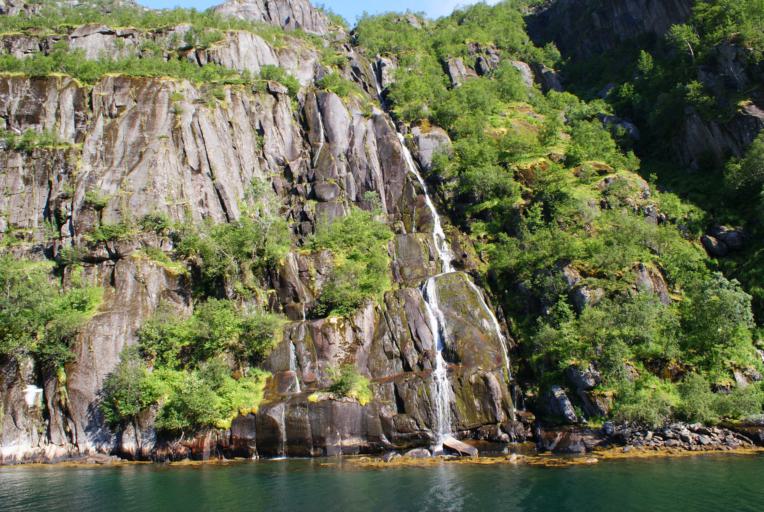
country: NO
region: Nordland
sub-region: Hadsel
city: Melbu
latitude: 68.3645
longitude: 14.9472
